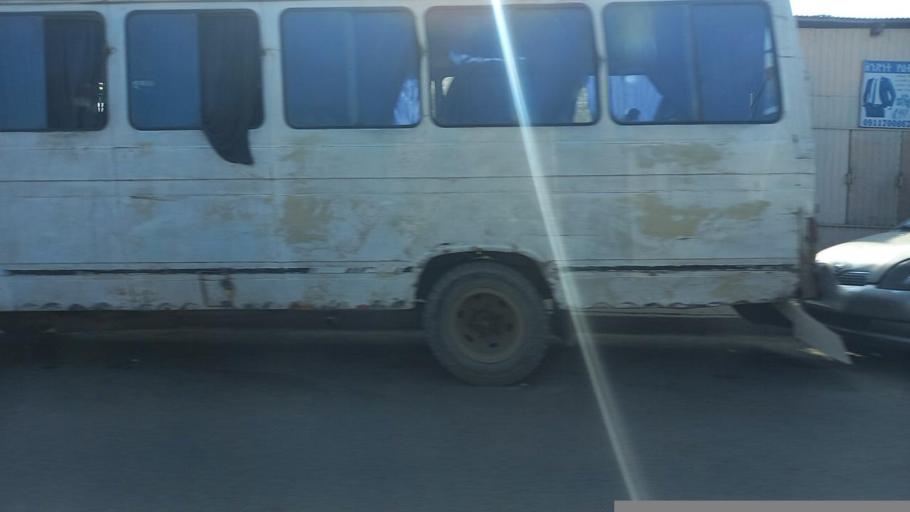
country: ET
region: Adis Abeba
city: Addis Ababa
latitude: 8.9377
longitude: 38.7468
